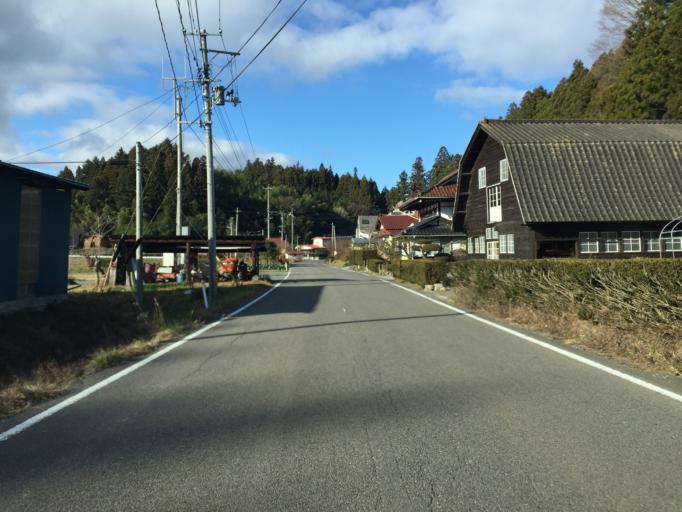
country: JP
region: Fukushima
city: Ishikawa
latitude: 37.2182
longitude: 140.5986
